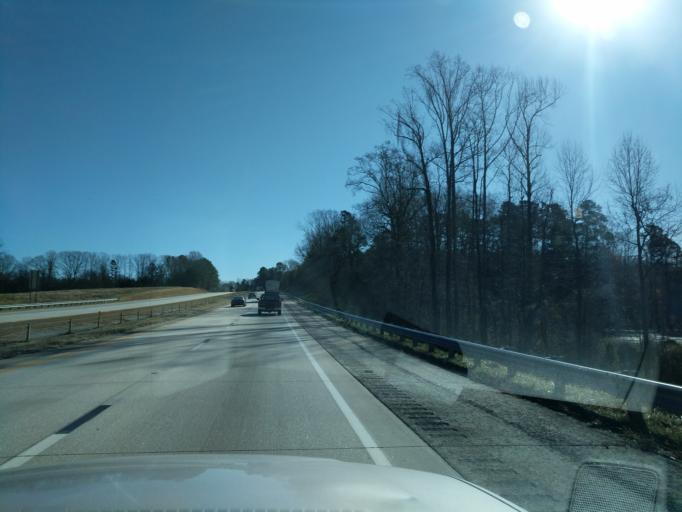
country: US
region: South Carolina
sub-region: Laurens County
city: Clinton
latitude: 34.5206
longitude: -81.9102
